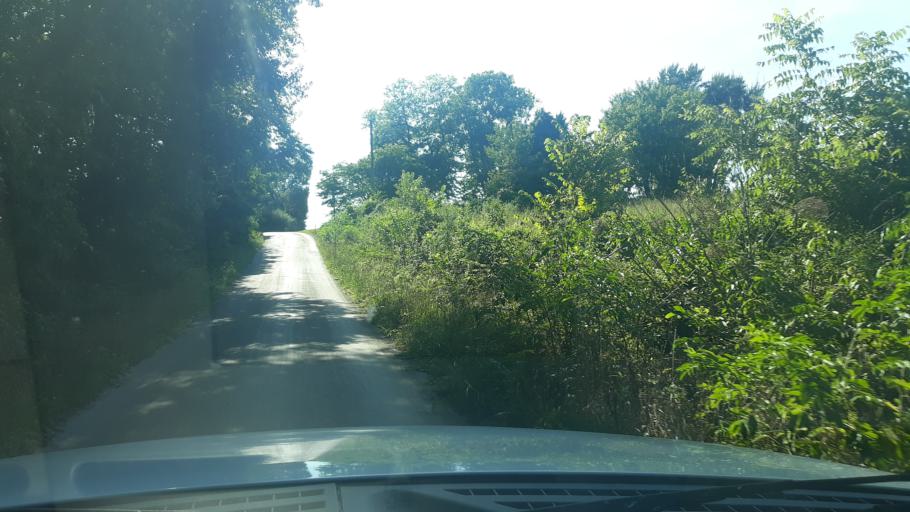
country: US
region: Illinois
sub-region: Saline County
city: Harrisburg
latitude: 37.8524
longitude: -88.5980
